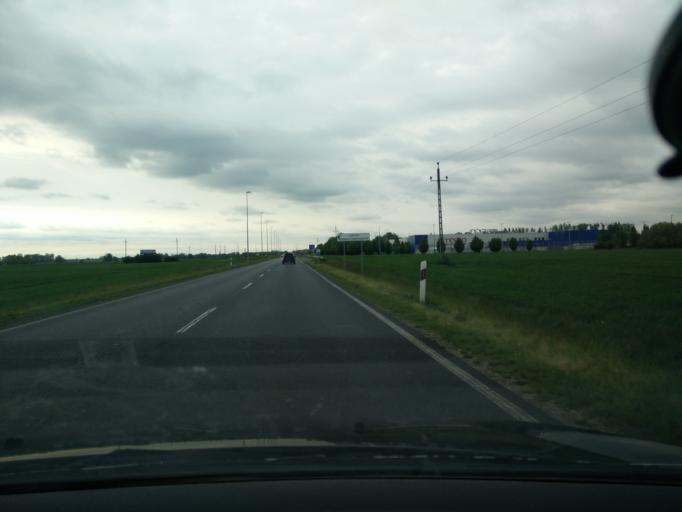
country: HU
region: Veszprem
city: Papa
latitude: 47.3185
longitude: 17.4512
